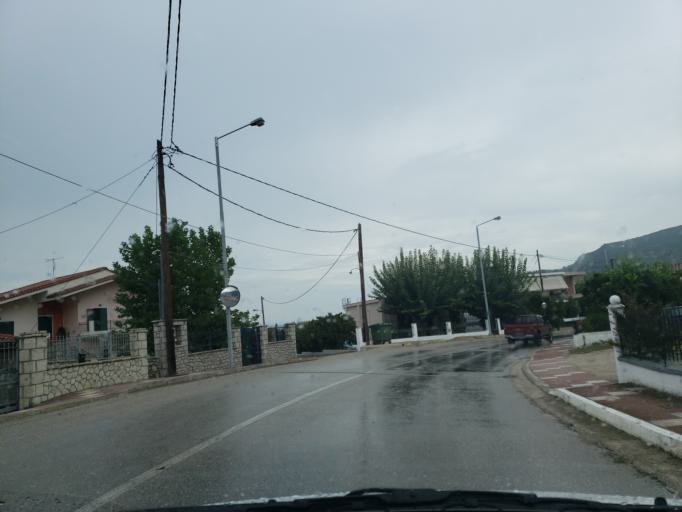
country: GR
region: Central Greece
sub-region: Nomos Fthiotidos
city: Anthili
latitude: 38.7997
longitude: 22.4702
